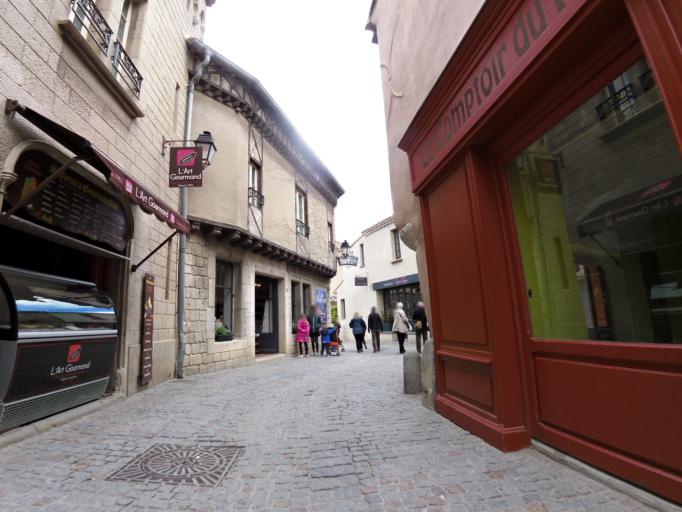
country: FR
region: Languedoc-Roussillon
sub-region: Departement de l'Aude
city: Carcassonne
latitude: 43.2060
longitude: 2.3632
